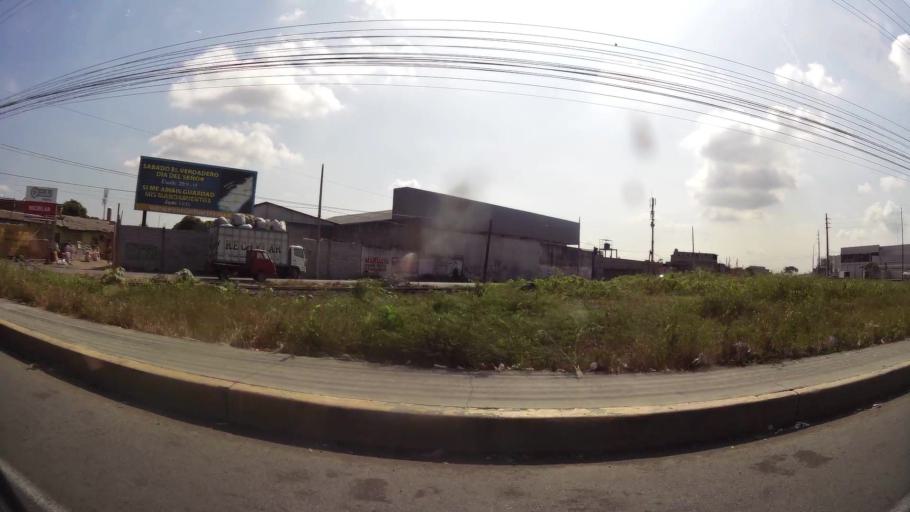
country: EC
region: Guayas
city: Eloy Alfaro
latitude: -2.1768
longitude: -79.8279
